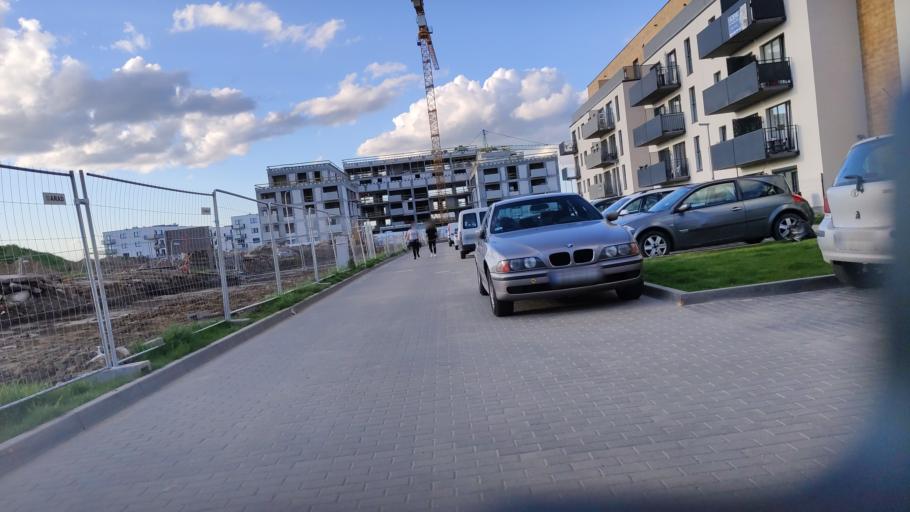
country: PL
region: Lower Silesian Voivodeship
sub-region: Powiat wroclawski
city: Zerniki Wroclawskie
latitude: 51.0548
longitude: 17.0523
